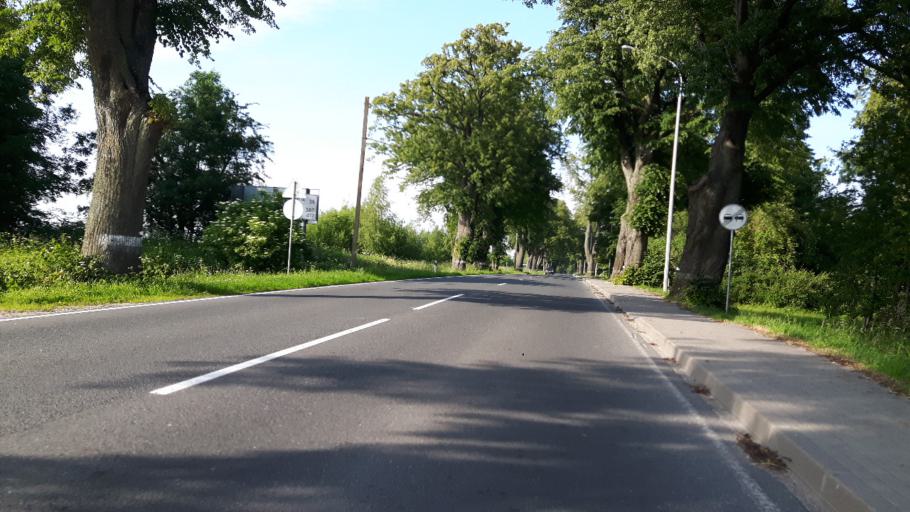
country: RU
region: Kaliningrad
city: Ladushkin
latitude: 54.5053
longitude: 20.0996
